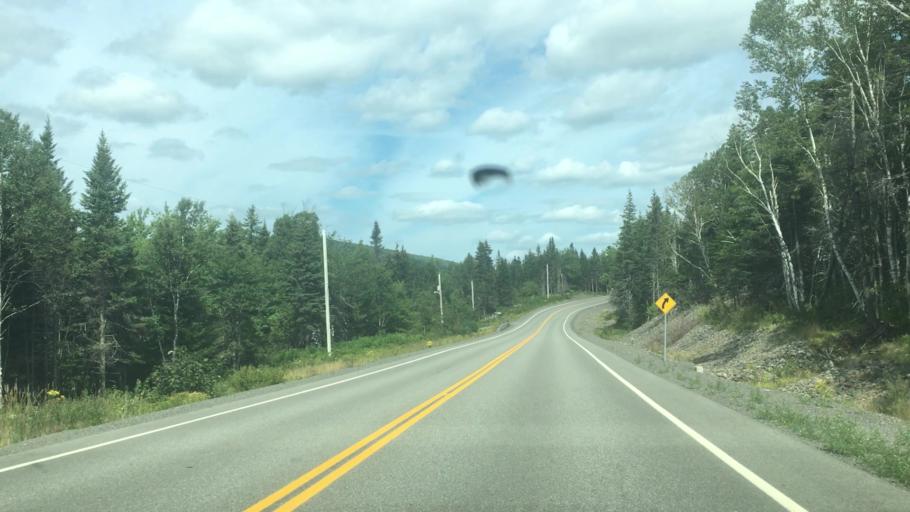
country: CA
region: Nova Scotia
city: Sydney Mines
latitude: 46.3246
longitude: -60.6066
